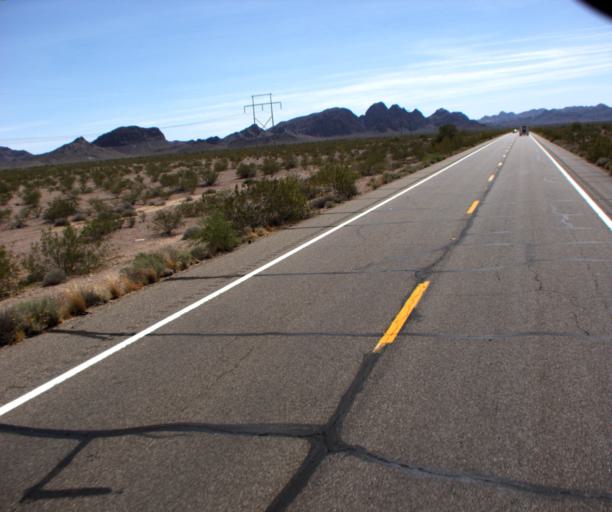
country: US
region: Arizona
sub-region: La Paz County
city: Quartzsite
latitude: 33.3286
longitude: -114.2170
